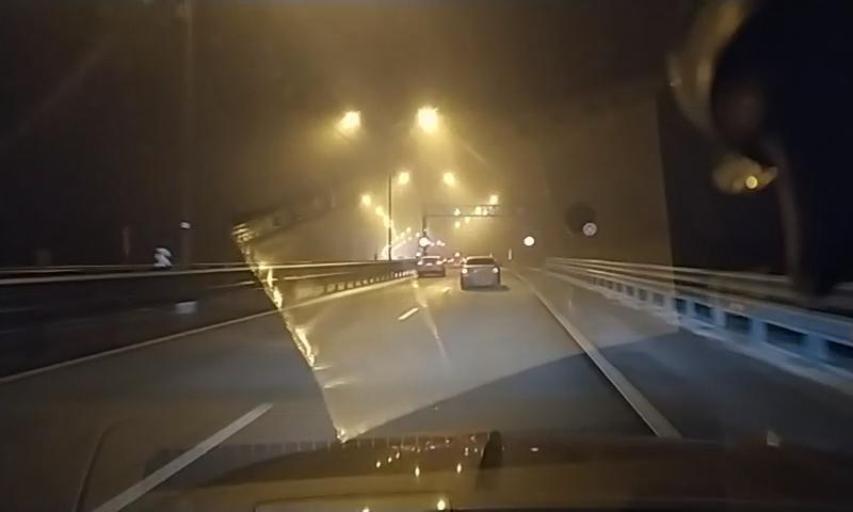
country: RU
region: Leningrad
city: Bugry
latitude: 60.1157
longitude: 30.3865
